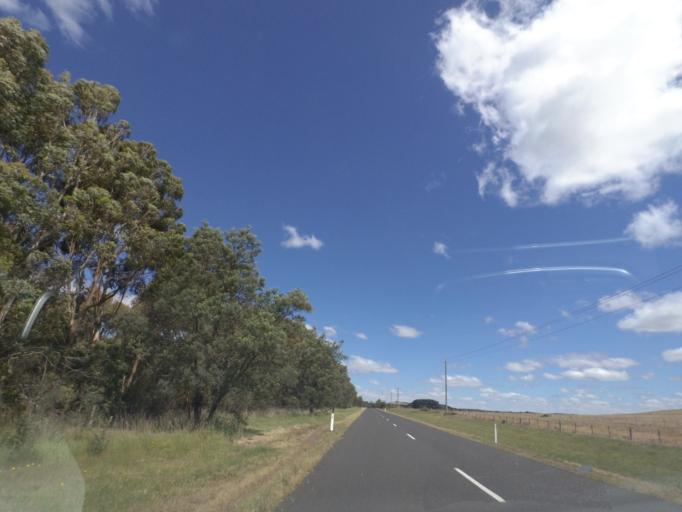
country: AU
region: Victoria
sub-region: Hume
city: Sunbury
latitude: -37.3128
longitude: 144.5186
